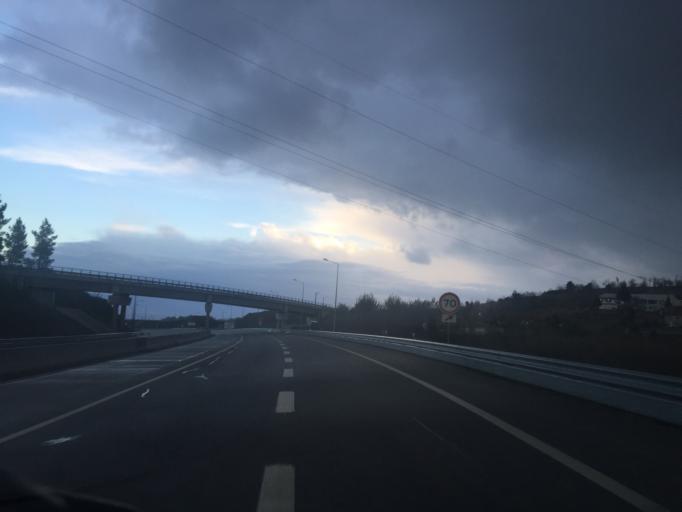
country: PT
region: Guarda
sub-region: Trancoso
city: Trancoso
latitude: 40.7573
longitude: -7.3289
